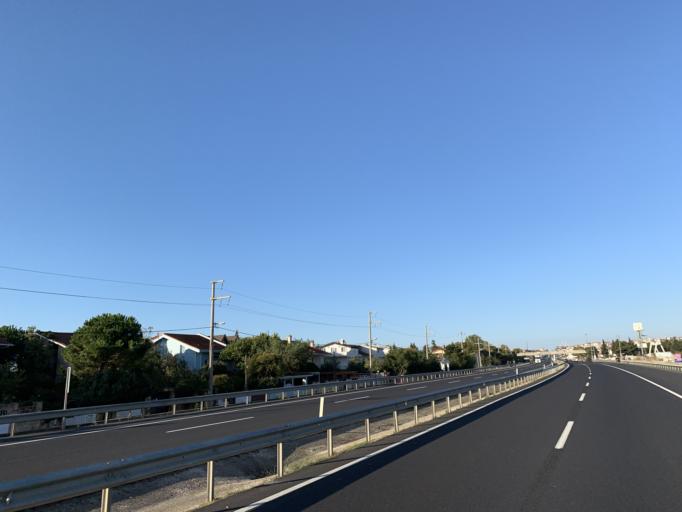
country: TR
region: Istanbul
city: Canta
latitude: 41.0565
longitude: 28.0701
